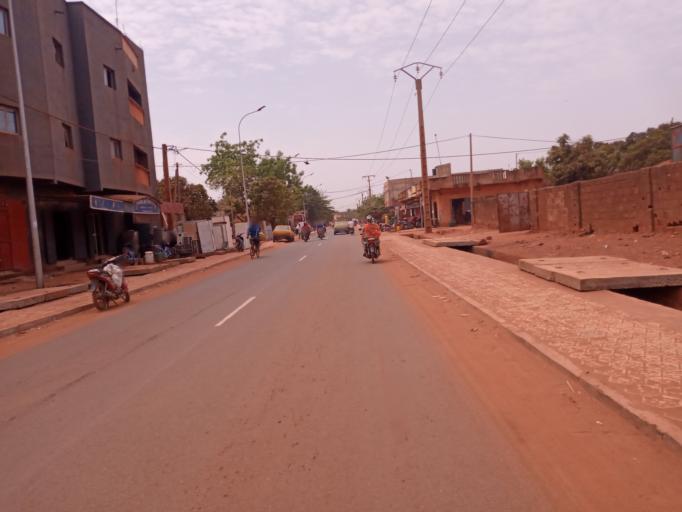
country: ML
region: Bamako
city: Bamako
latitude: 12.5824
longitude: -7.9882
